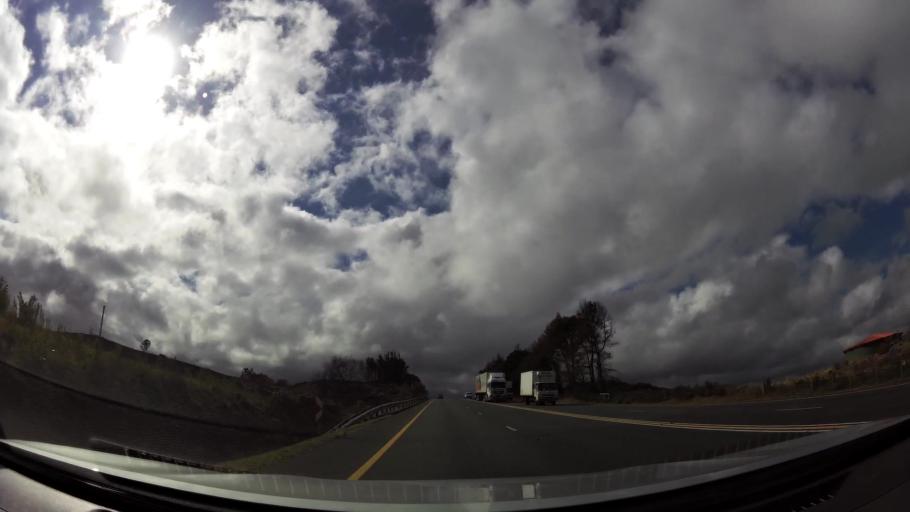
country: ZA
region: Western Cape
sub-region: Eden District Municipality
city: Knysna
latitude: -34.0386
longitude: 23.1210
